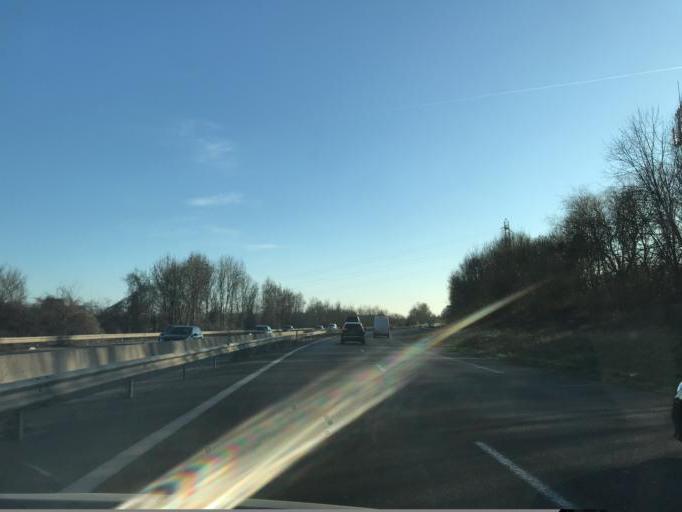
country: FR
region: Ile-de-France
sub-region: Departement de Seine-et-Marne
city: Lesigny
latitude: 48.7393
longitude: 2.6127
